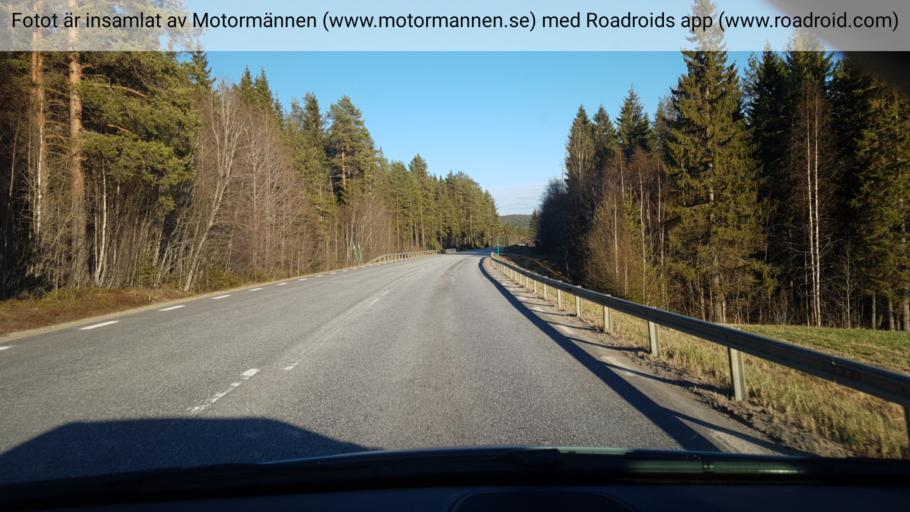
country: SE
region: Vaesterbotten
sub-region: Vannas Kommun
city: Vaennaes
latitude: 63.9675
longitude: 19.7438
